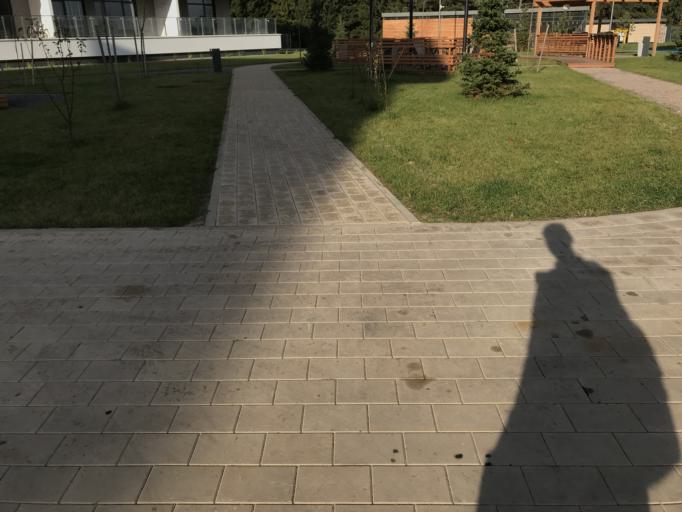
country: BY
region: Minsk
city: Khatsyezhyna
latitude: 53.9475
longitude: 27.3309
